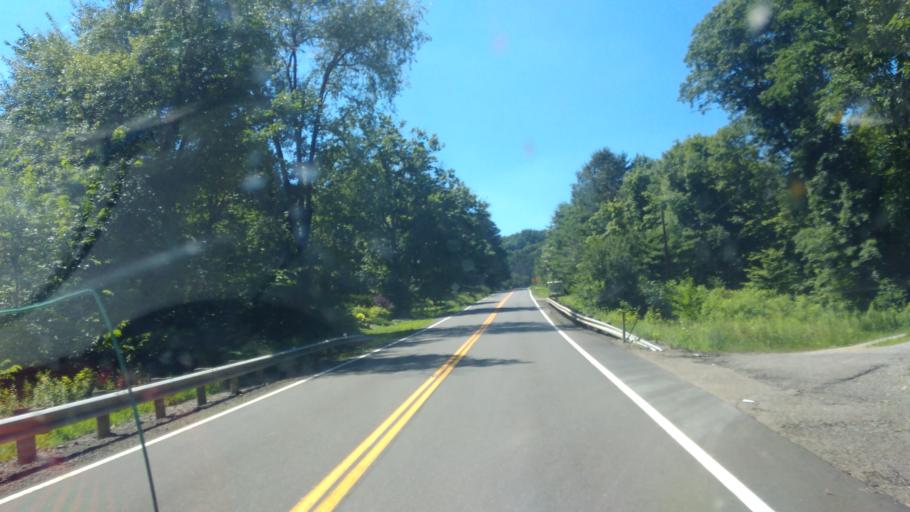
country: US
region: Ohio
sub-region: Columbiana County
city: Salineville
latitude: 40.4831
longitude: -80.9359
